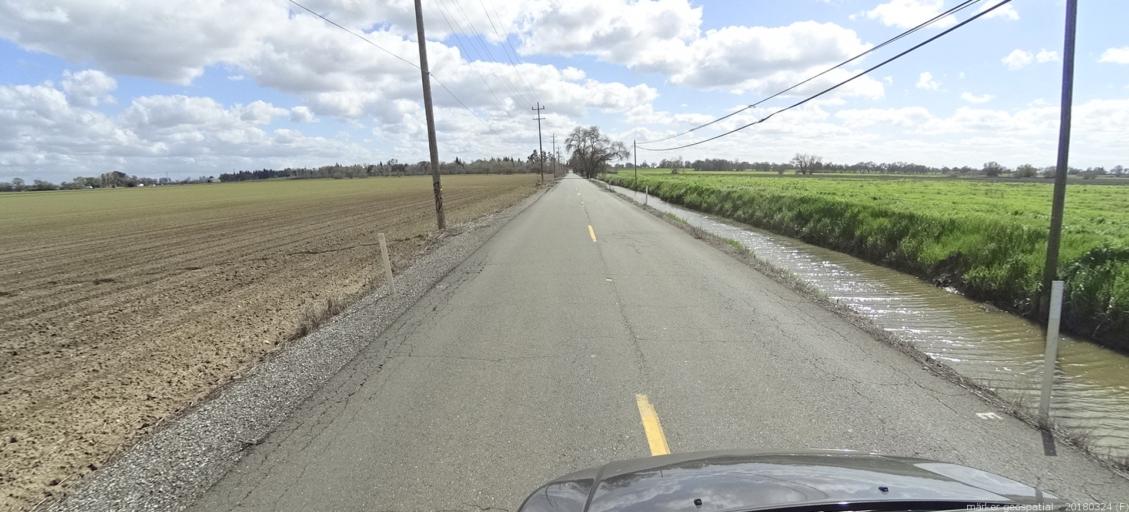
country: US
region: California
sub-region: Yolo County
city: West Sacramento
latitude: 38.6611
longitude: -121.5767
